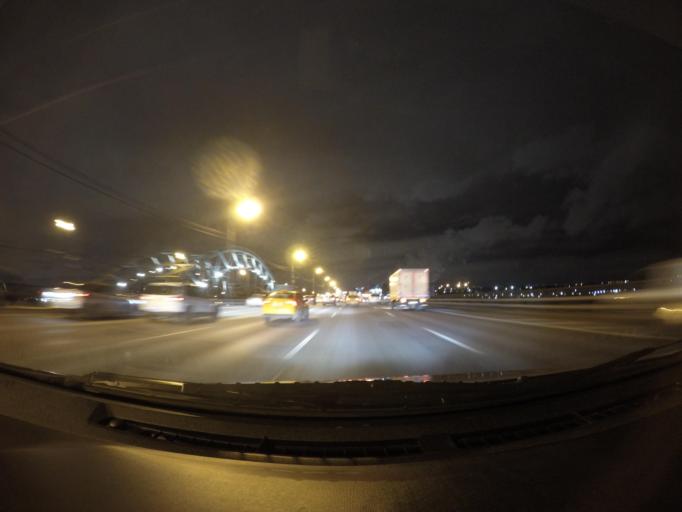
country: RU
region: Moskovskaya
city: Alekseyevka
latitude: 55.6227
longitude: 37.7926
